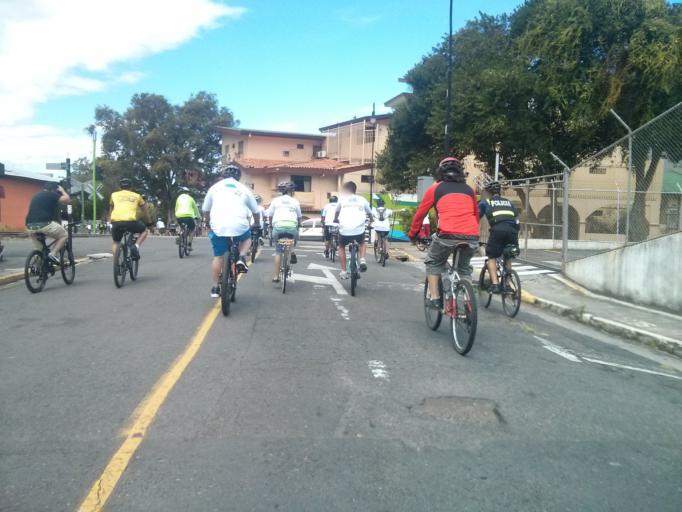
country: CR
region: San Jose
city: Calle Blancos
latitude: 9.9377
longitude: -84.0707
